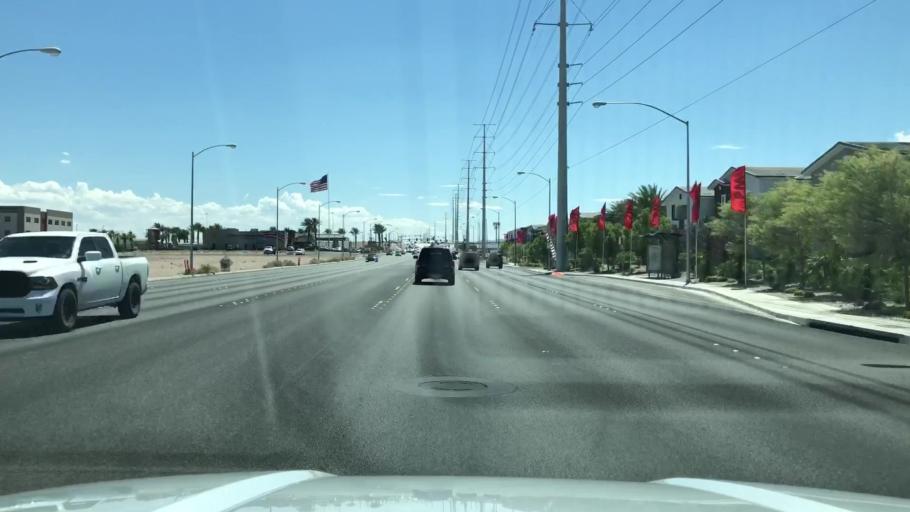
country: US
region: Nevada
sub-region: Clark County
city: Spring Valley
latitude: 36.0740
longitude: -115.2795
